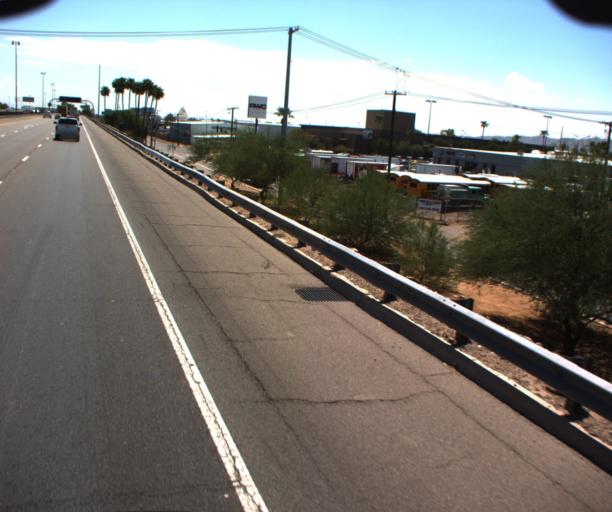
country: US
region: Arizona
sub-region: Maricopa County
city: Phoenix
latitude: 33.4286
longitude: -112.0756
